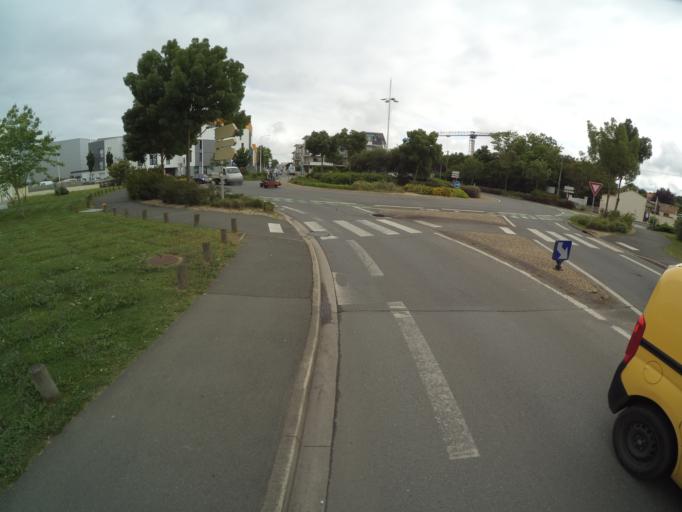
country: FR
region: Poitou-Charentes
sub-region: Departement de la Charente-Maritime
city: La Rochelle
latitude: 46.1457
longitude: -1.1526
